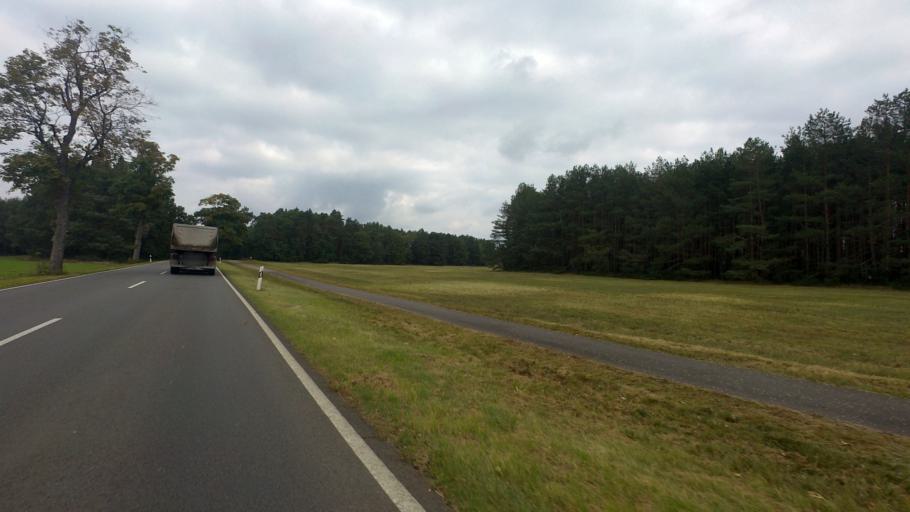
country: DE
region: Brandenburg
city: Schilda
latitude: 51.5802
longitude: 13.3575
